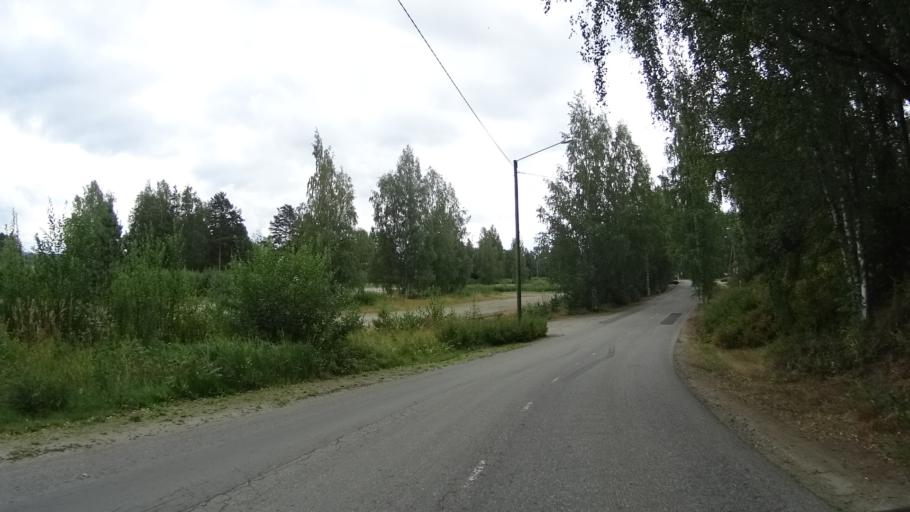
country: FI
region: Pirkanmaa
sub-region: Tampere
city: Kangasala
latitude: 61.4449
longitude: 24.1282
